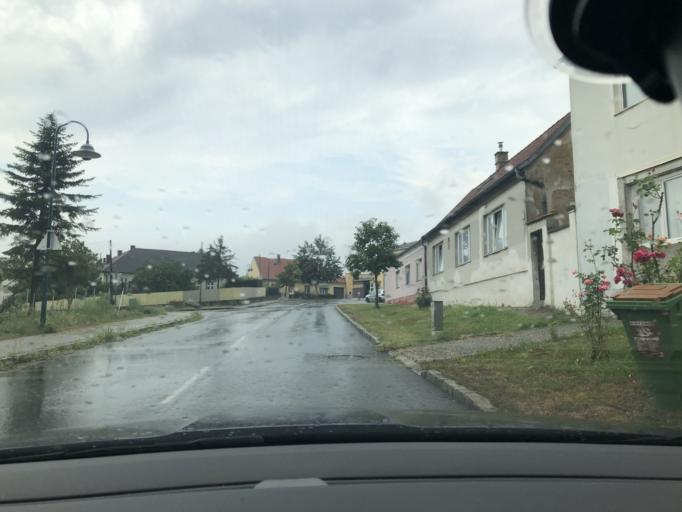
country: AT
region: Lower Austria
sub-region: Politischer Bezirk Ganserndorf
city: Gross-Schweinbarth
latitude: 48.3928
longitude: 16.6569
